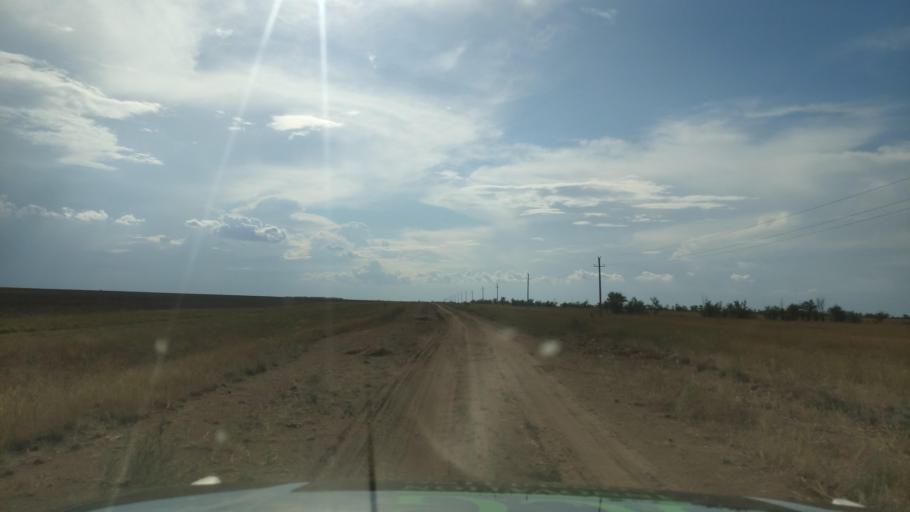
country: KZ
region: Pavlodar
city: Pavlodar
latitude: 52.5126
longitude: 77.4834
